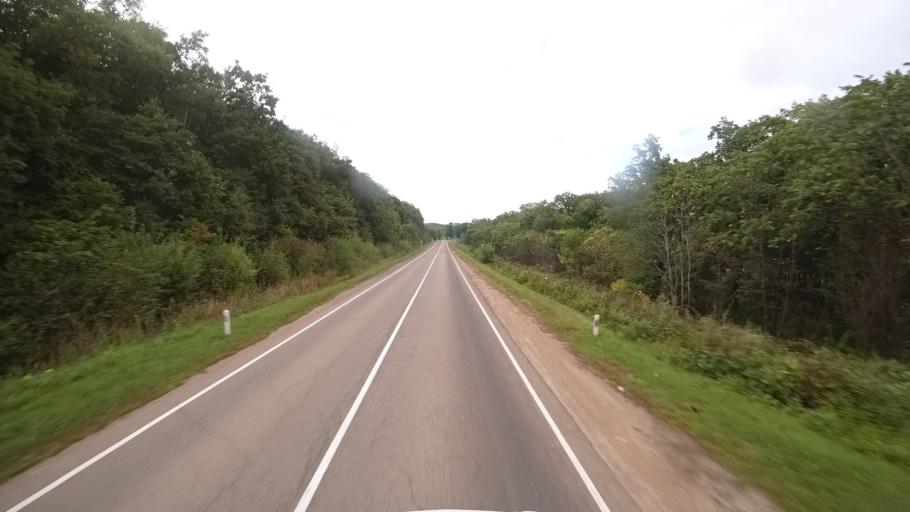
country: RU
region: Primorskiy
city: Yakovlevka
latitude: 44.3963
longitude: 133.4676
